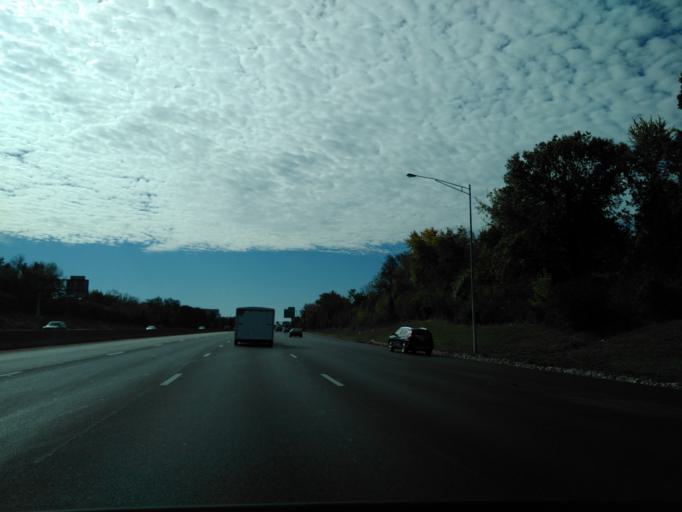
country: US
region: Missouri
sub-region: Saint Louis County
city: Creve Coeur
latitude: 38.6537
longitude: -90.4482
